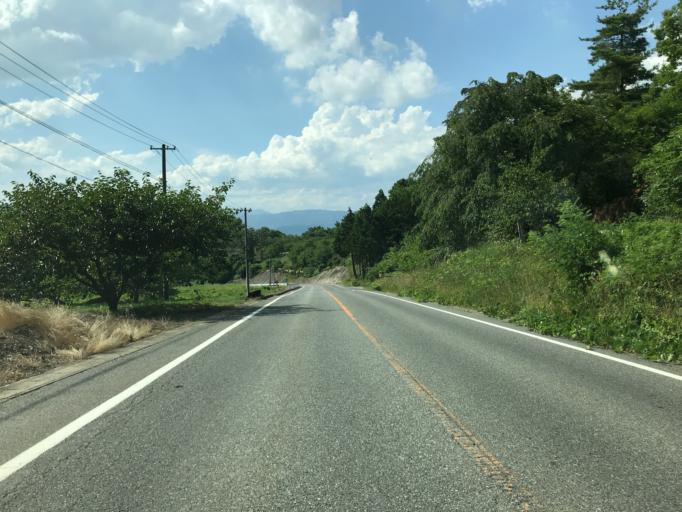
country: JP
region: Fukushima
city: Yanagawamachi-saiwaicho
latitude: 37.8140
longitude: 140.5948
